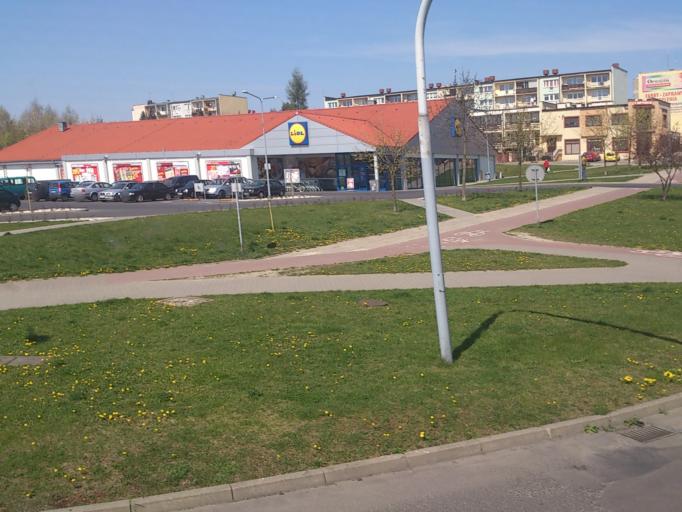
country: PL
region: Lodz Voivodeship
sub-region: Piotrkow Trybunalski
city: Piotrkow Trybunalski
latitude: 51.4048
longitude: 19.6680
